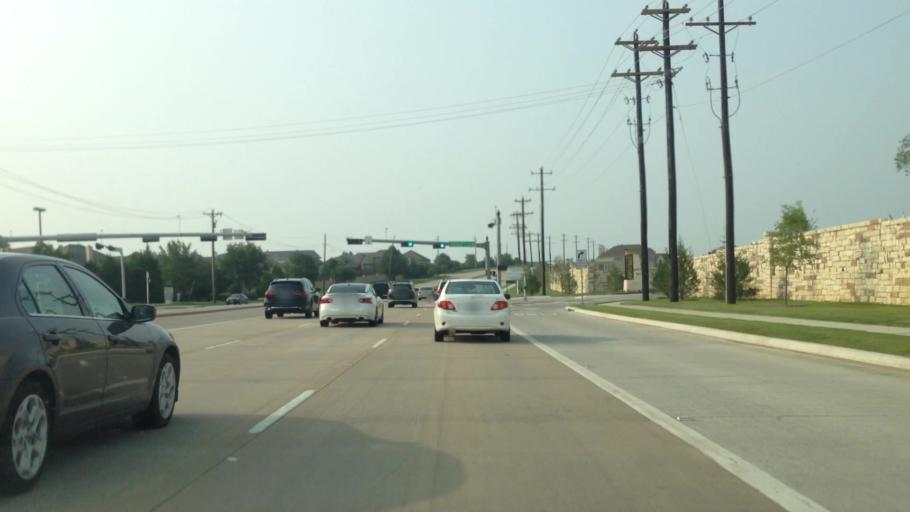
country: US
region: Texas
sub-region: Denton County
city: The Colony
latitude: 33.0298
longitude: -96.9176
